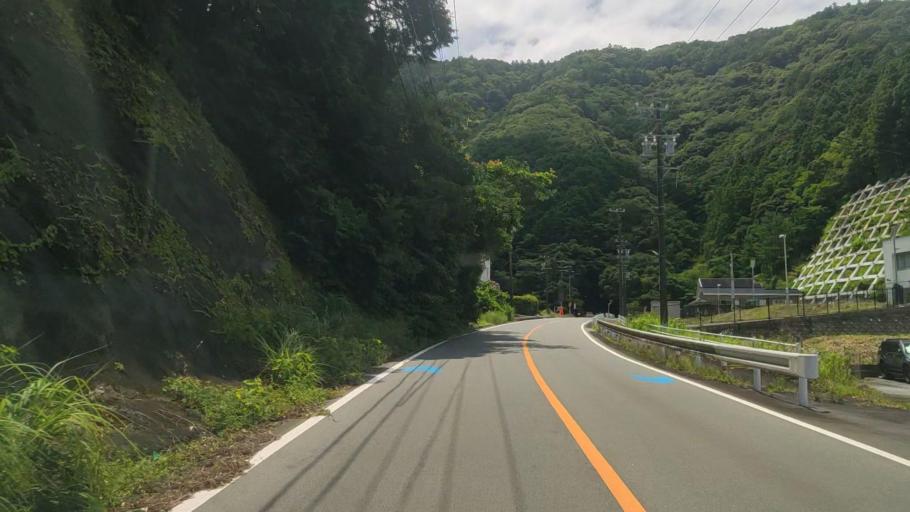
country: JP
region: Mie
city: Ise
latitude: 34.2737
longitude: 136.4918
